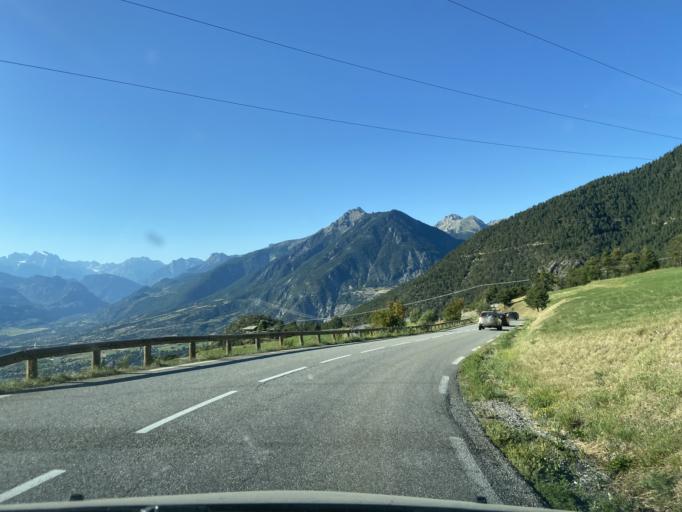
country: FR
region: Provence-Alpes-Cote d'Azur
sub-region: Departement des Hautes-Alpes
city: Guillestre
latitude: 44.6351
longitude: 6.6696
